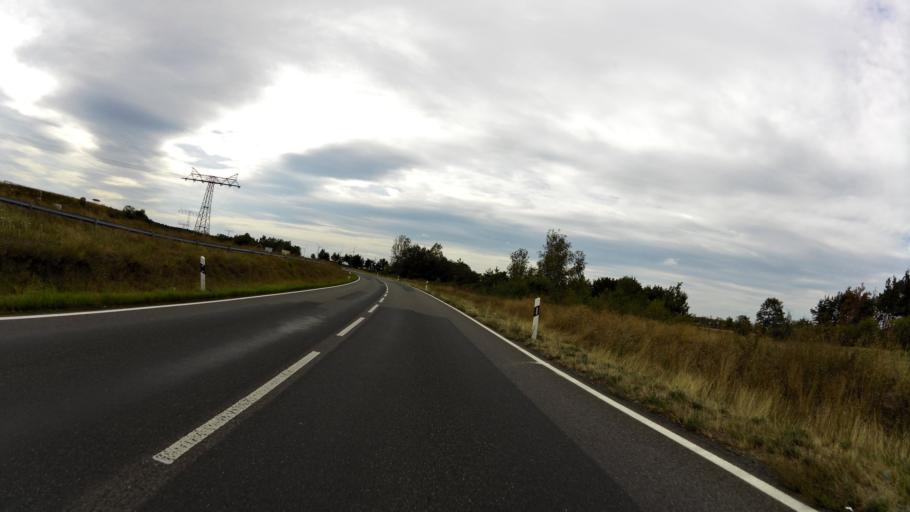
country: DE
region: Brandenburg
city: Heinersbruck
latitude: 51.8138
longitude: 14.5086
